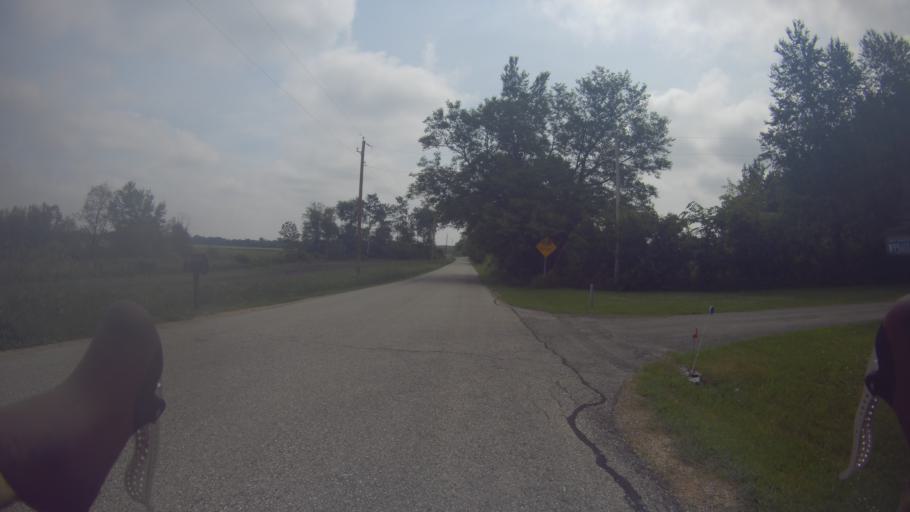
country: US
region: Wisconsin
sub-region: Jefferson County
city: Cambridge
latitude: 42.9237
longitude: -89.0069
